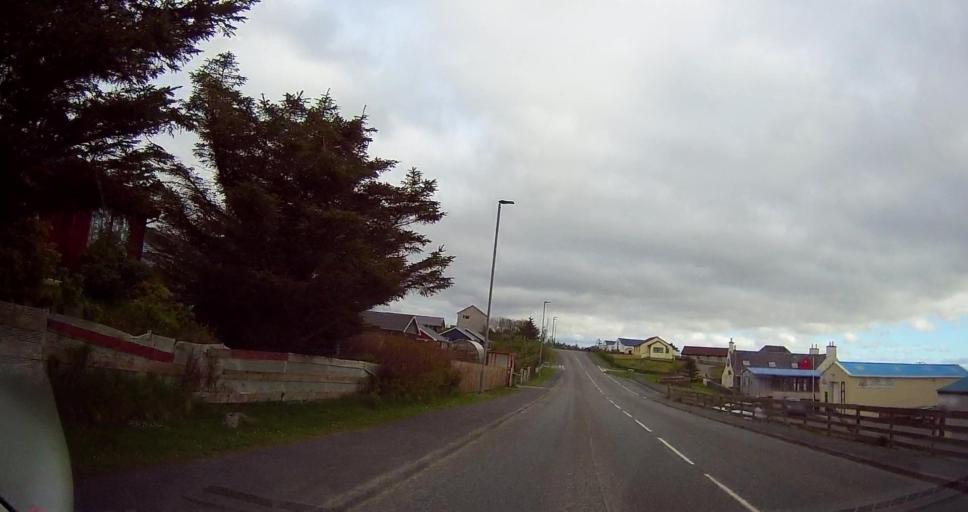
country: GB
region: Scotland
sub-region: Shetland Islands
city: Lerwick
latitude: 60.3901
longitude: -1.3488
